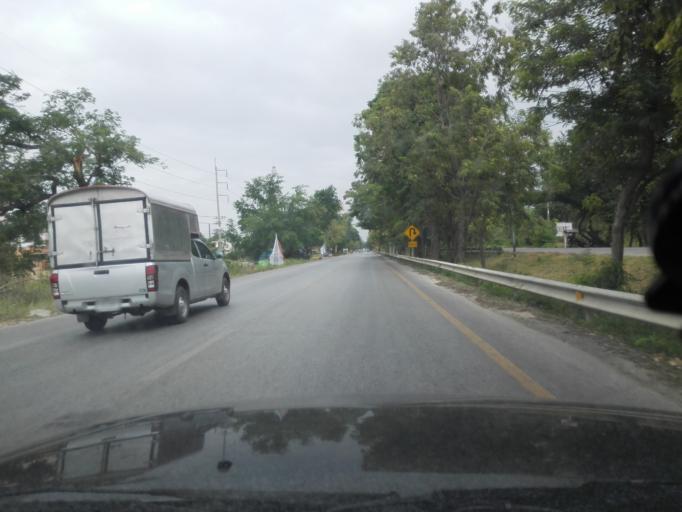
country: TH
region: Nakhon Sawan
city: Nakhon Sawan
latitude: 15.7291
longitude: 100.0369
